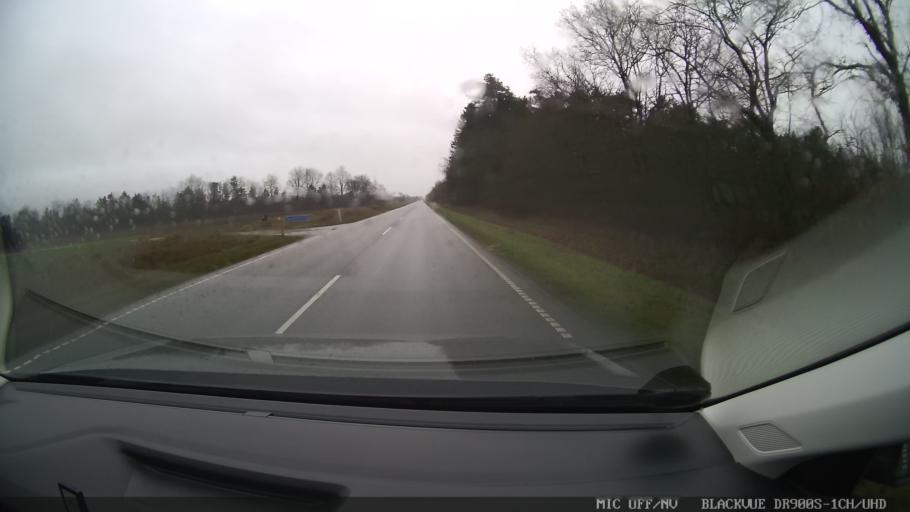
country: DK
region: Central Jutland
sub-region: Herning Kommune
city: Sunds
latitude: 56.2894
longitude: 8.9191
